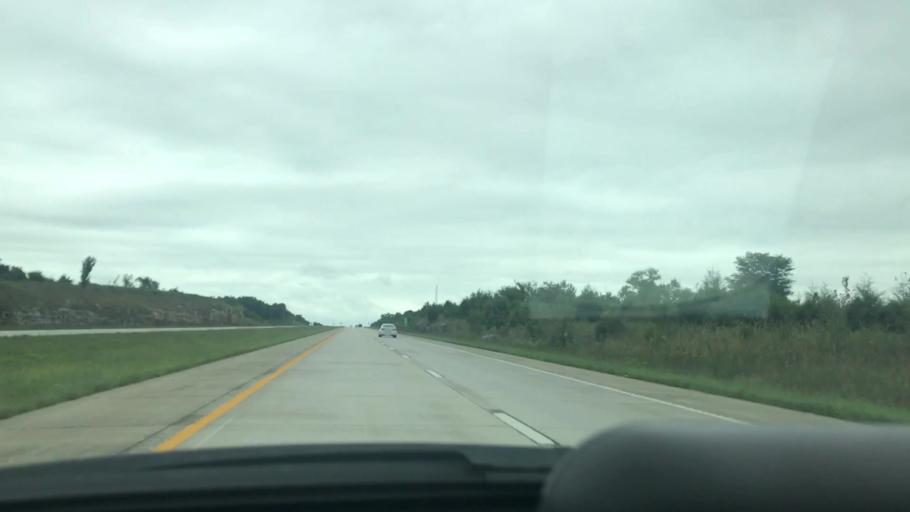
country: US
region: Missouri
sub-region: Dallas County
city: Buffalo
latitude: 37.5338
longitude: -93.1372
